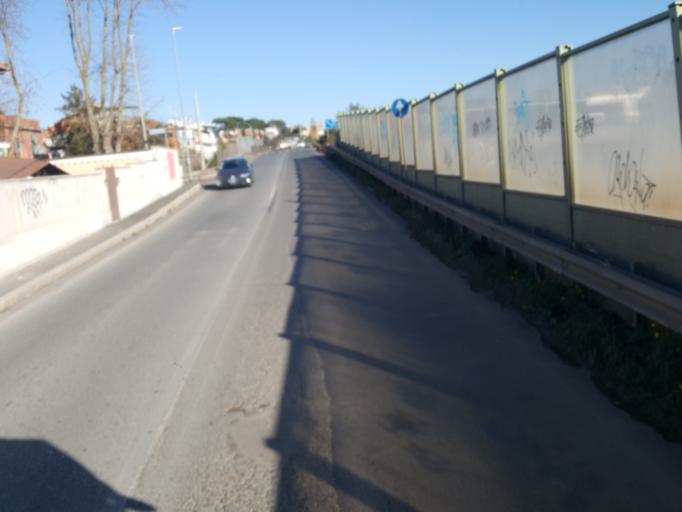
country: IT
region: Latium
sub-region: Citta metropolitana di Roma Capitale
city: Acilia-Castel Fusano-Ostia Antica
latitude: 41.7814
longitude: 12.3552
